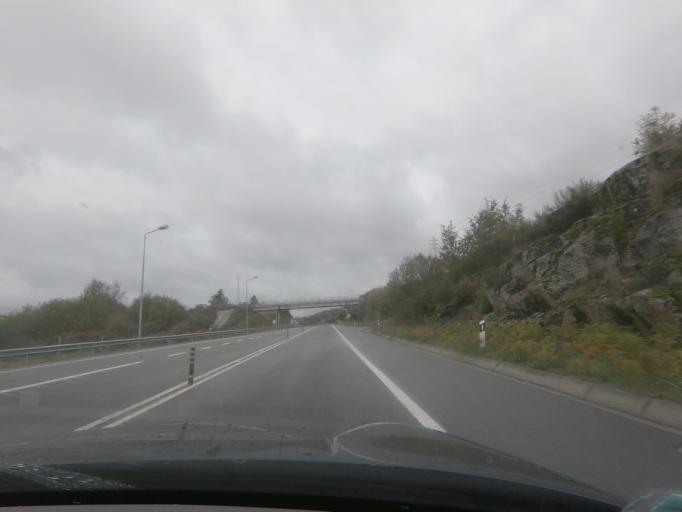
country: PT
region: Vila Real
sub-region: Vila Real
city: Vila Real
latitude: 41.2846
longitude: -7.8167
